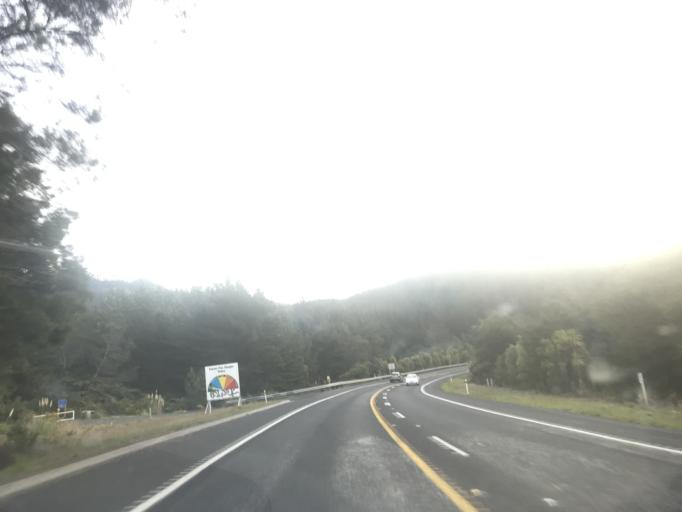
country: NZ
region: Bay of Plenty
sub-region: Western Bay of Plenty District
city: Waihi Beach
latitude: -37.4627
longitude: 175.9168
